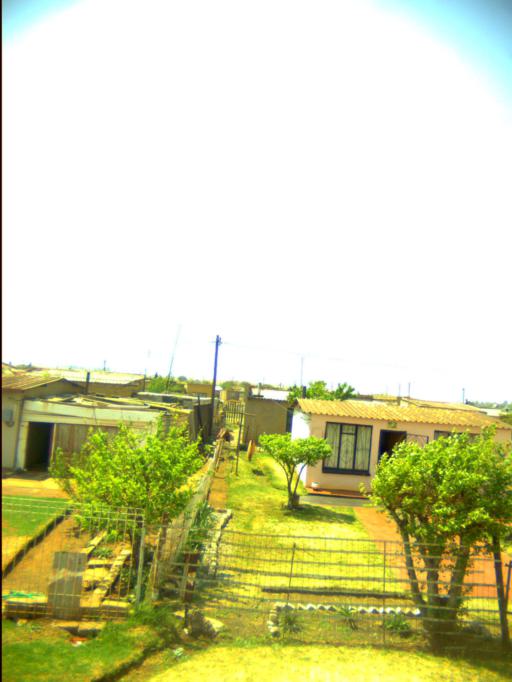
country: ZA
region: Mpumalanga
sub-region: Nkangala District Municipality
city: Delmas
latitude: -26.1414
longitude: 28.6911
